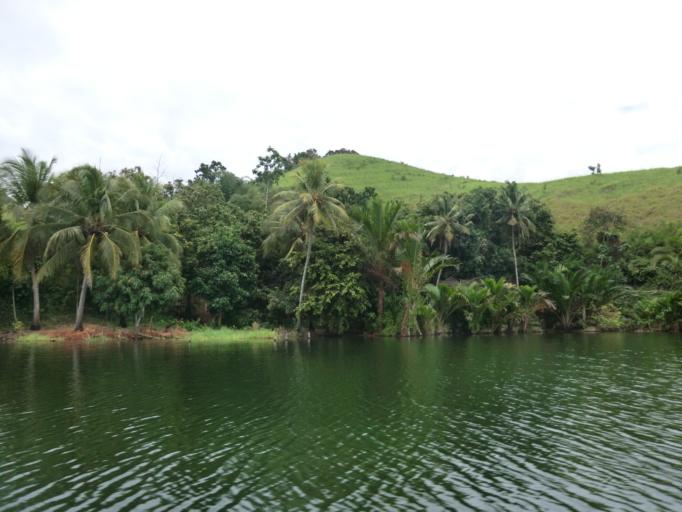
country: ID
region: Papua
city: Sentani
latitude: -2.6031
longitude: 140.5388
